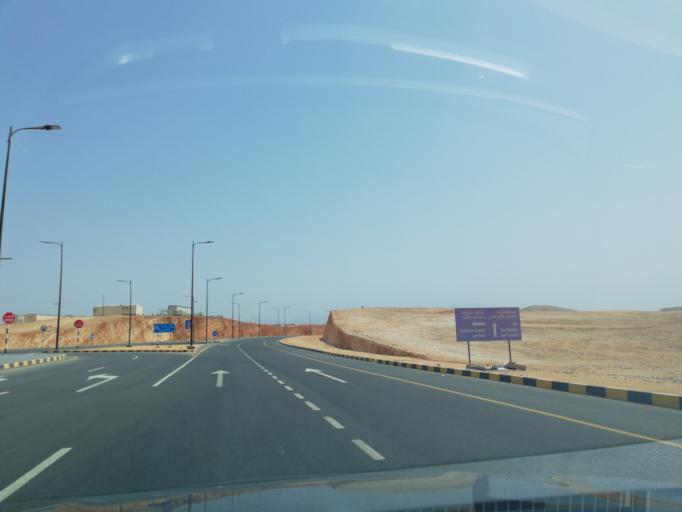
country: OM
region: Muhafazat Masqat
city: Bawshar
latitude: 23.5674
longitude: 58.3211
